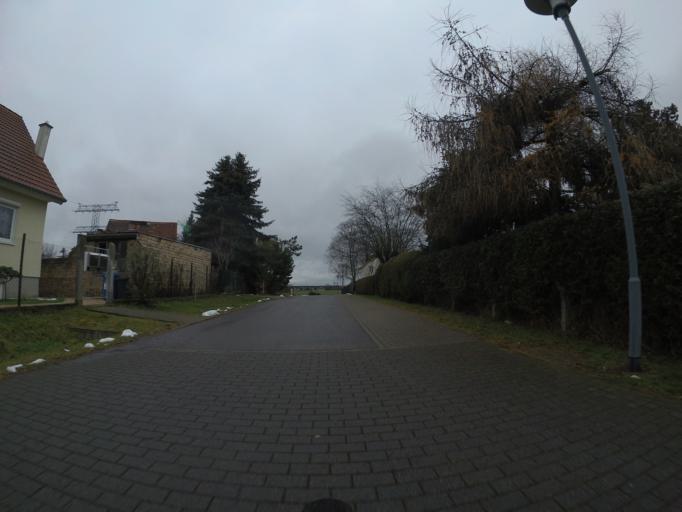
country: DE
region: Brandenburg
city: Ahrensfelde
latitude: 52.5683
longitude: 13.5866
